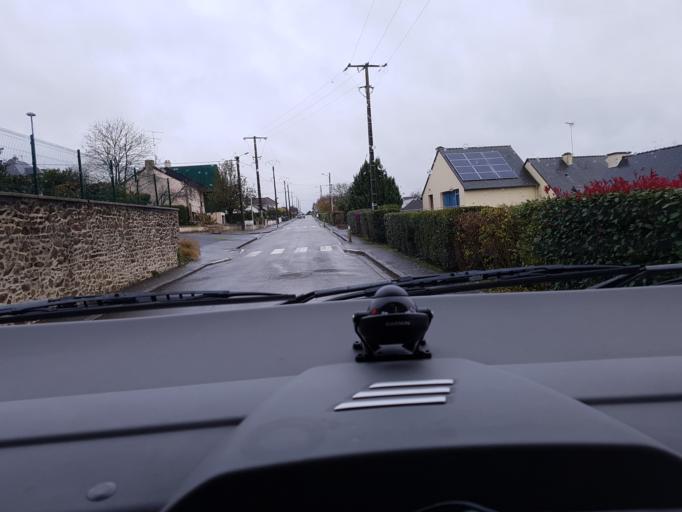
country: FR
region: Pays de la Loire
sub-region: Departement de la Mayenne
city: Montenay
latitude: 48.2888
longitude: -0.8922
